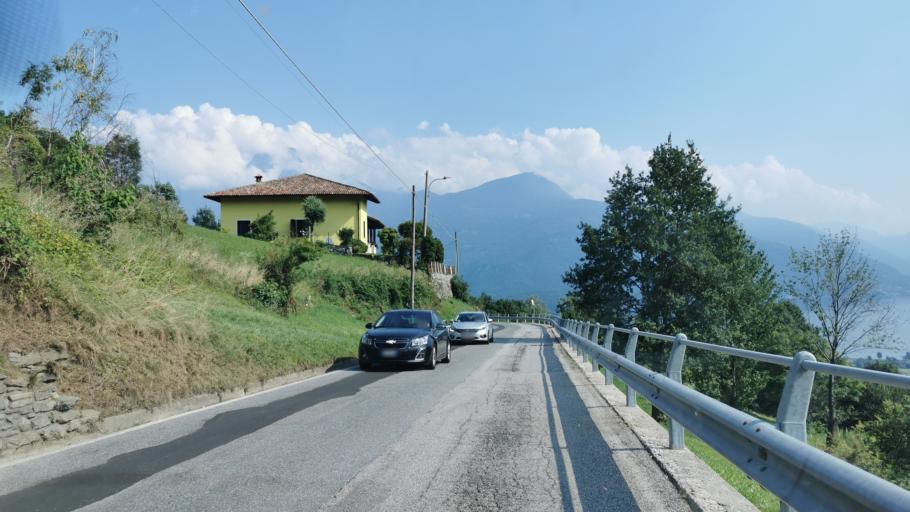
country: IT
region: Lombardy
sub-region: Provincia di Como
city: Peglio
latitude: 46.1558
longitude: 9.2933
